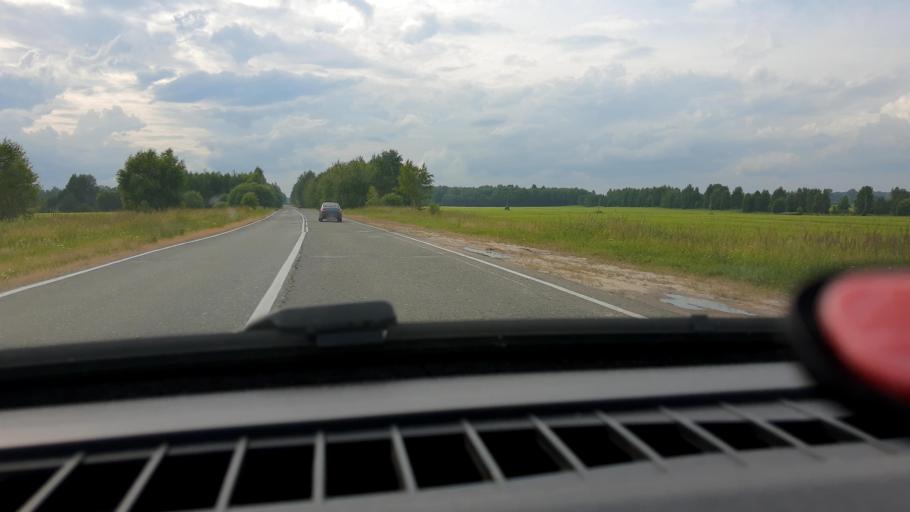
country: RU
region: Nizjnij Novgorod
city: Neklyudovo
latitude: 56.5065
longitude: 43.9719
